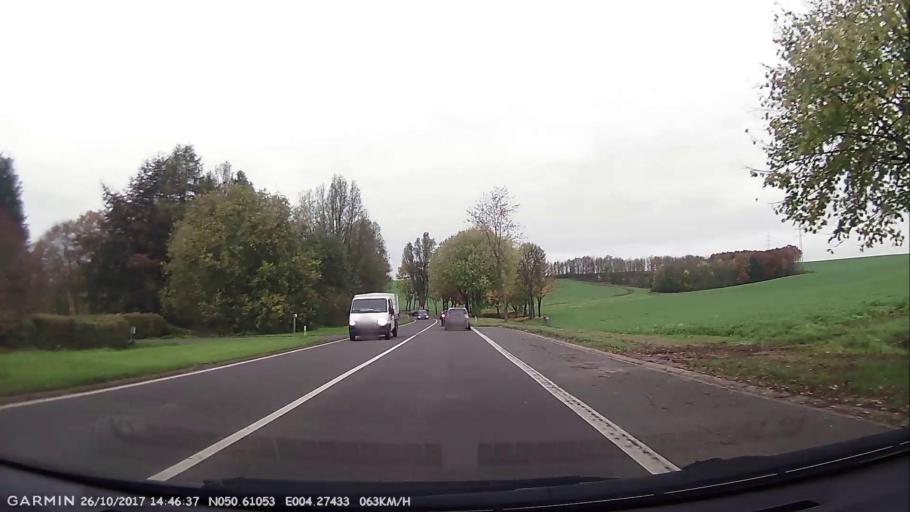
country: BE
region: Wallonia
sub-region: Province du Brabant Wallon
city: Ittre
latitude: 50.6106
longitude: 4.2742
